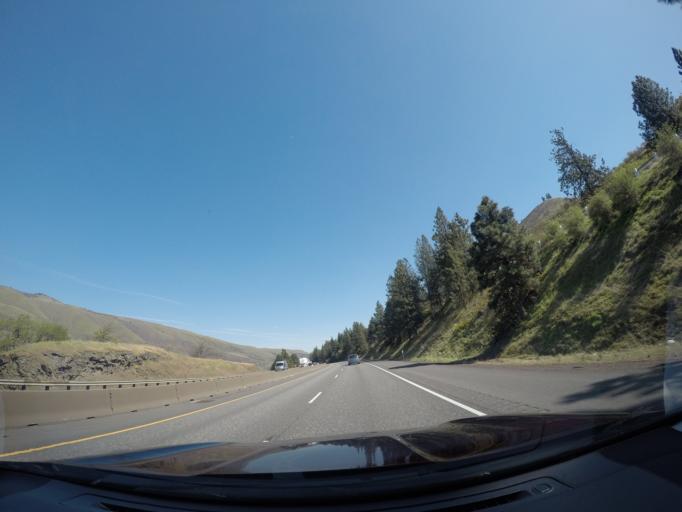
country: US
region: Oregon
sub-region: Wasco County
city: Chenoweth
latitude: 45.6694
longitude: -121.2506
